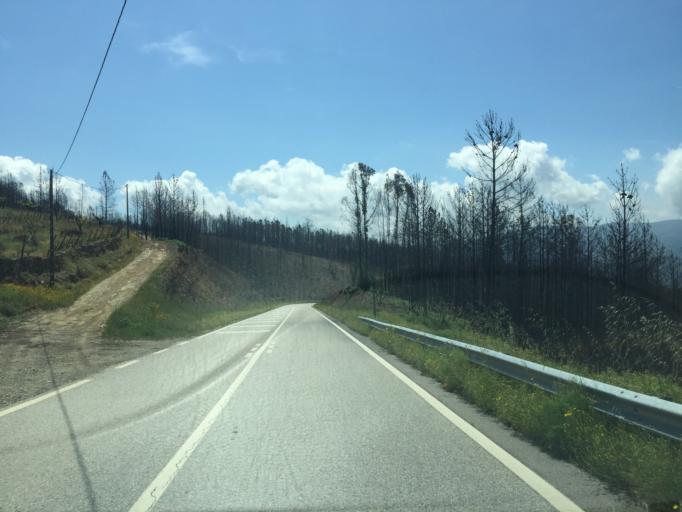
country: PT
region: Coimbra
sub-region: Pampilhosa da Serra
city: Pampilhosa da Serra
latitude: 40.0048
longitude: -7.9780
